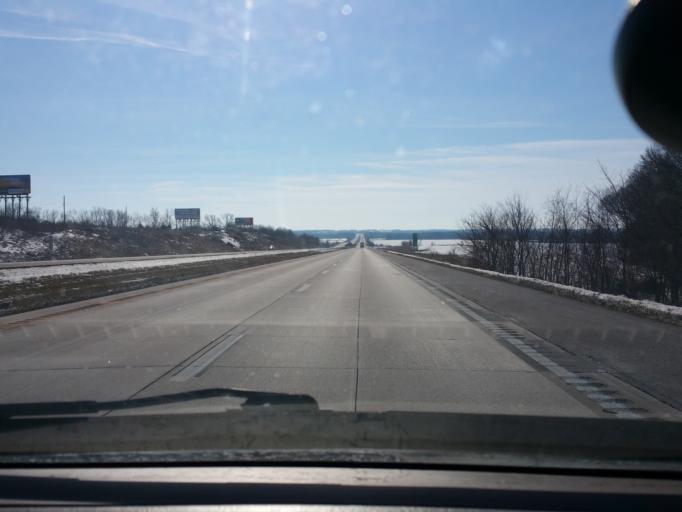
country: US
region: Missouri
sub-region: Daviess County
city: Gallatin
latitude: 40.0597
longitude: -94.0944
